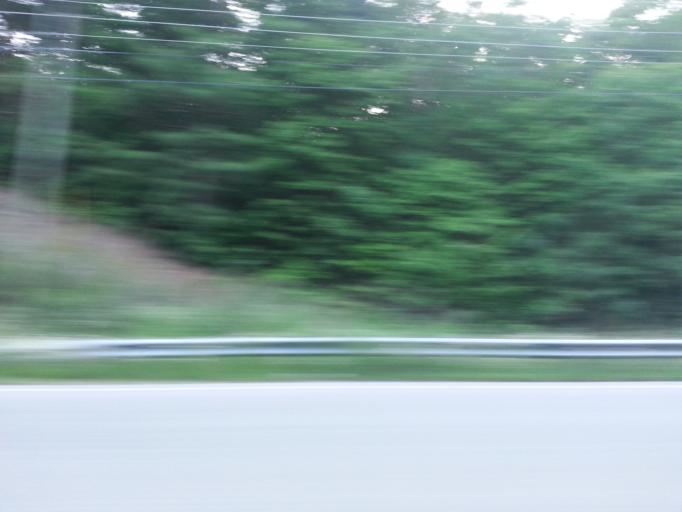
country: US
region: Tennessee
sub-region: Monroe County
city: Madisonville
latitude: 35.3205
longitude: -84.2971
